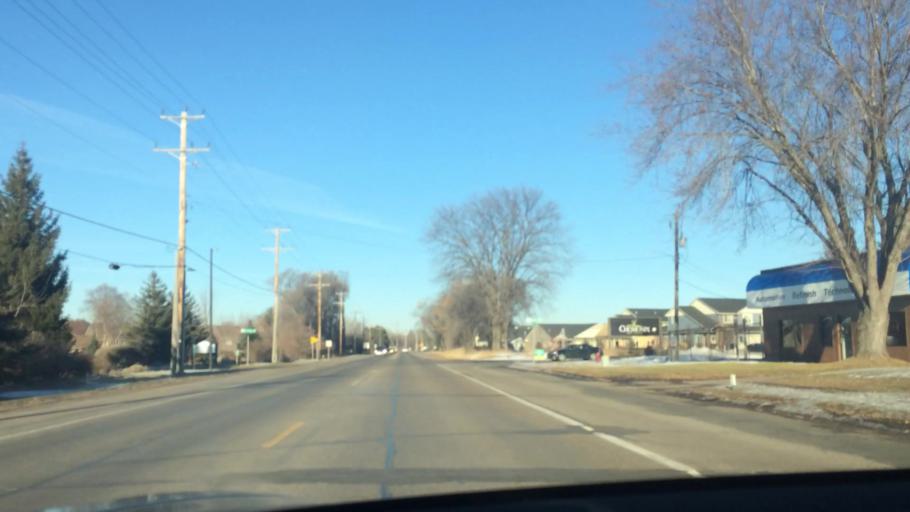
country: US
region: Minnesota
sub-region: Anoka County
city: Circle Pines
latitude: 45.1637
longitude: -93.1232
